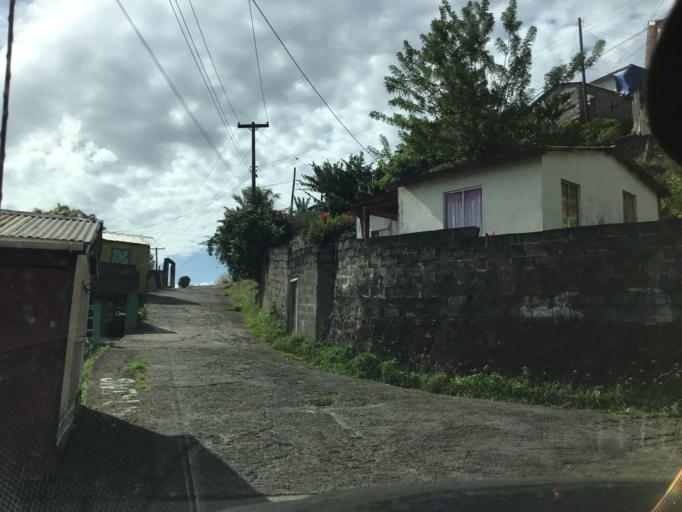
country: VC
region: Saint George
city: Kingstown
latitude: 13.1672
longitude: -61.2181
